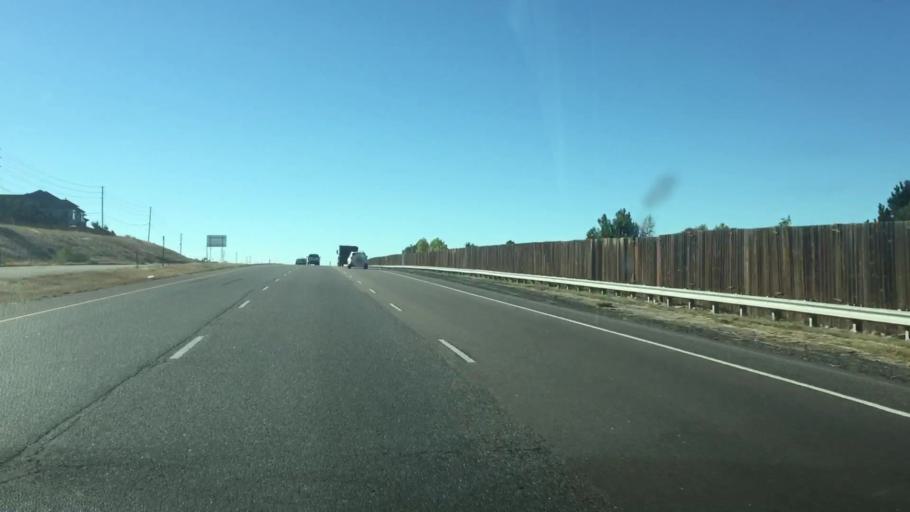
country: US
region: Colorado
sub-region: Douglas County
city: Parker
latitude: 39.4991
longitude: -104.7616
